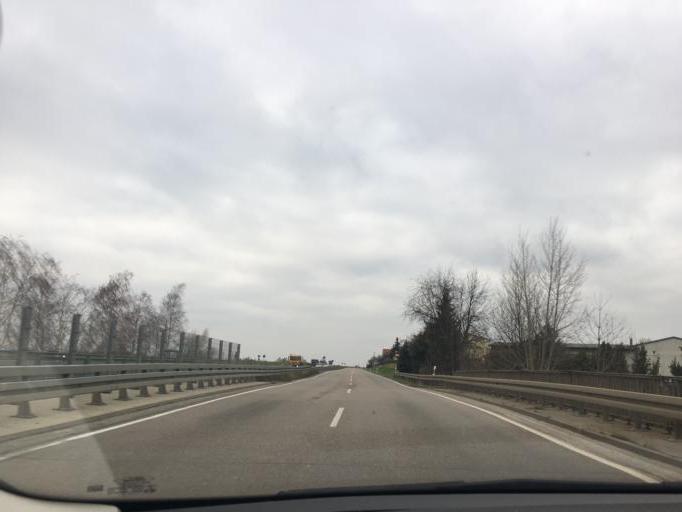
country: DE
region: Saxony
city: Borna
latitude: 51.1561
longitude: 12.5073
